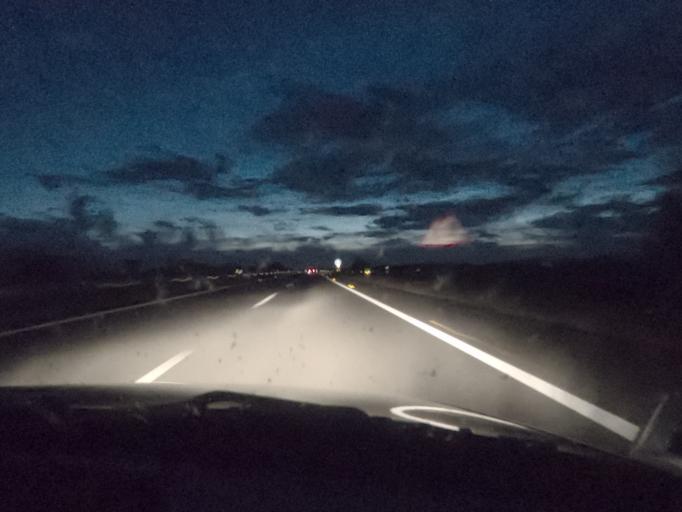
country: ES
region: Extremadura
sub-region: Provincia de Caceres
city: Morcillo
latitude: 39.9806
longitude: -6.3876
